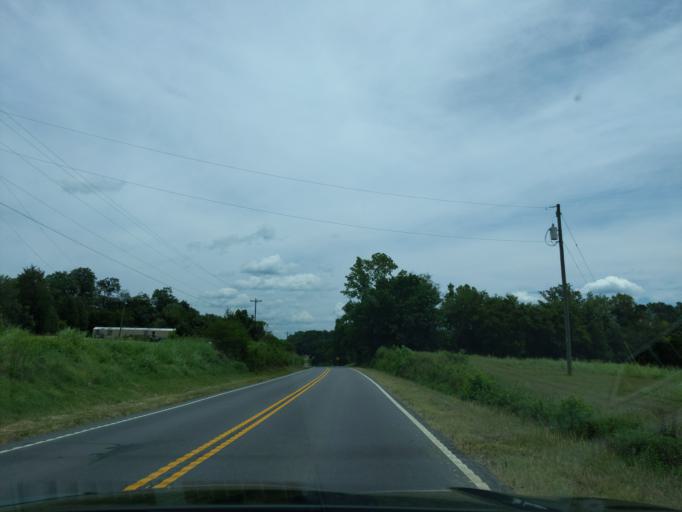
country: US
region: North Carolina
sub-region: Cabarrus County
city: Mount Pleasant
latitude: 35.4412
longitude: -80.3642
